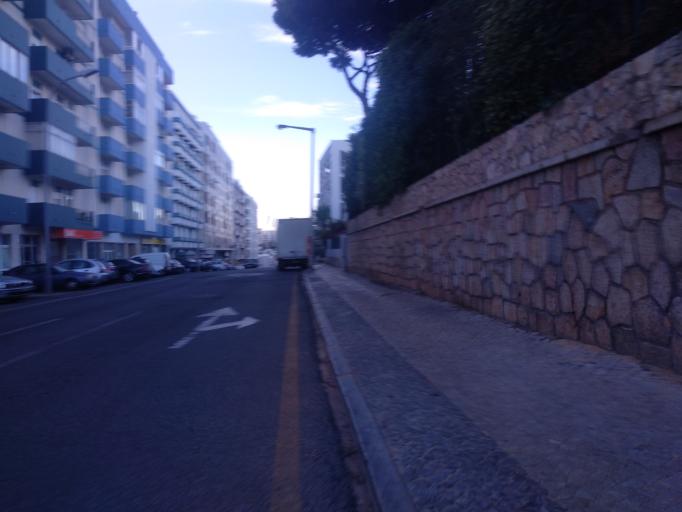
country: PT
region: Faro
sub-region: Faro
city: Faro
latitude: 37.0195
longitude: -7.9260
